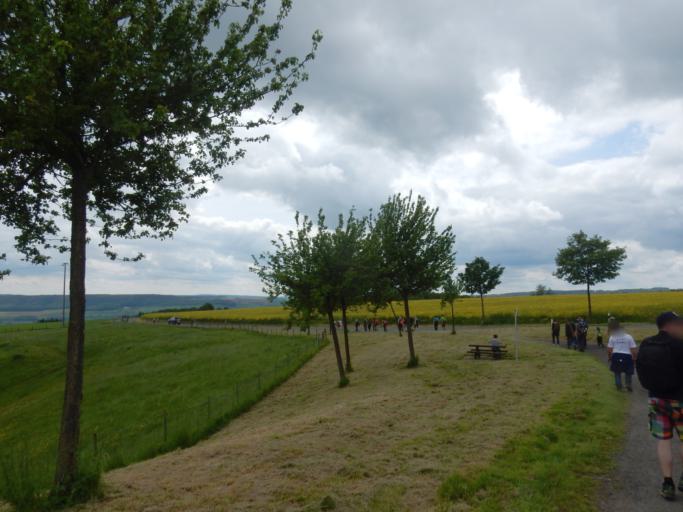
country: LU
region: Diekirch
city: Warken
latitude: 49.8746
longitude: 6.0939
